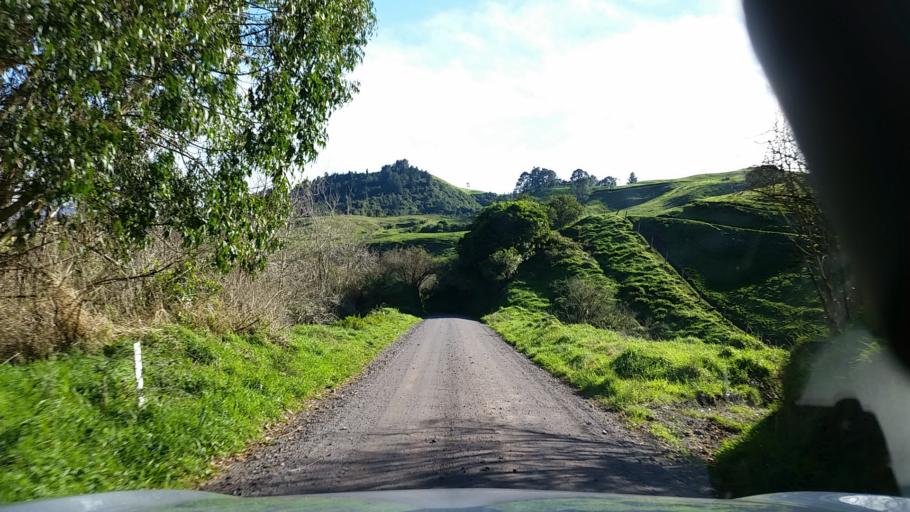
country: NZ
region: Waikato
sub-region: Taupo District
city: Taupo
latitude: -38.4317
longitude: 176.1579
